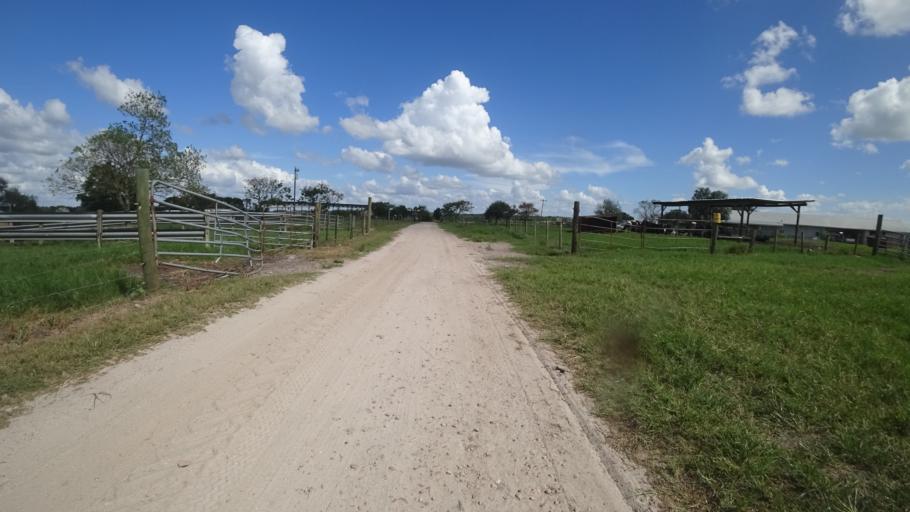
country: US
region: Florida
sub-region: Sarasota County
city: Warm Mineral Springs
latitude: 27.3142
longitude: -82.1319
